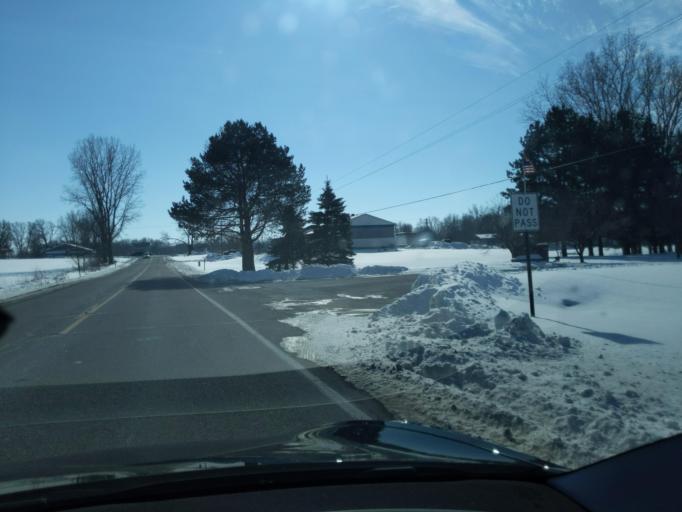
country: US
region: Michigan
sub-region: Livingston County
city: Fowlerville
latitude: 42.6012
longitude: -84.0709
